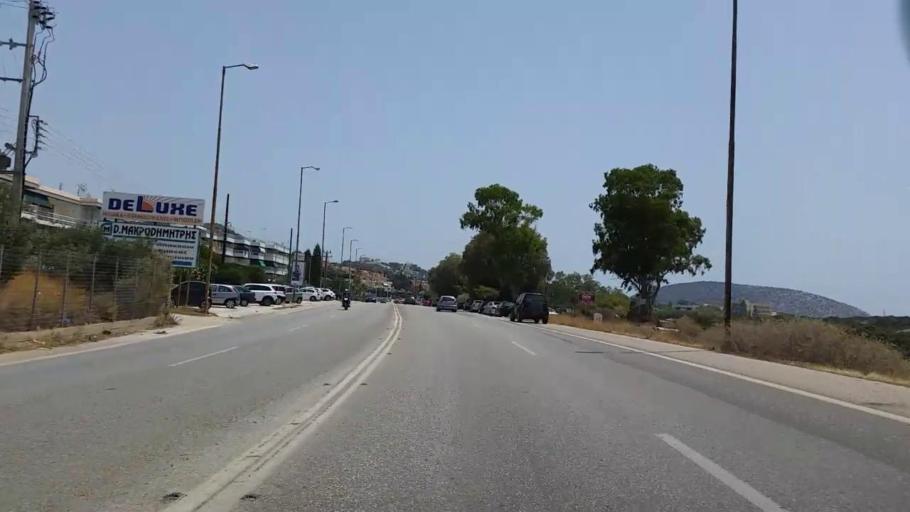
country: GR
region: Attica
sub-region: Nomarchia Anatolikis Attikis
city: Saronida
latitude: 37.7395
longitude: 23.9046
